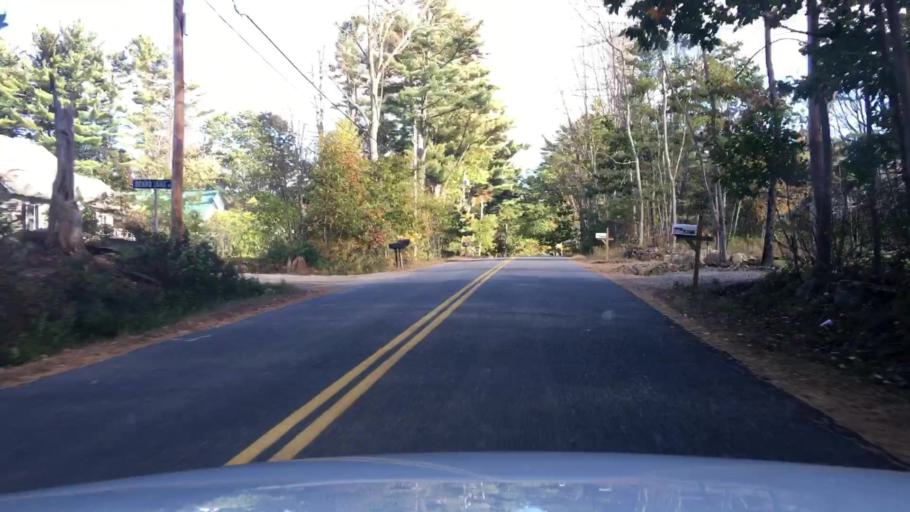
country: US
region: Maine
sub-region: York County
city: Wells Beach Station
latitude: 43.3353
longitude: -70.6286
